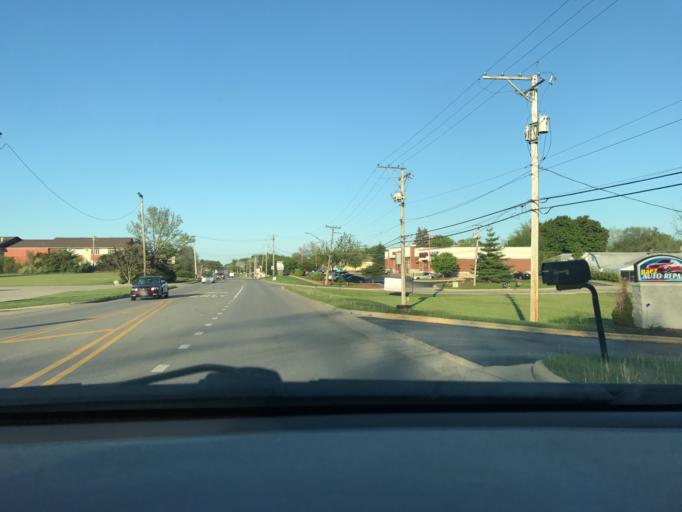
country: US
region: Illinois
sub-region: Kane County
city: Elgin
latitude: 42.0327
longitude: -88.3251
